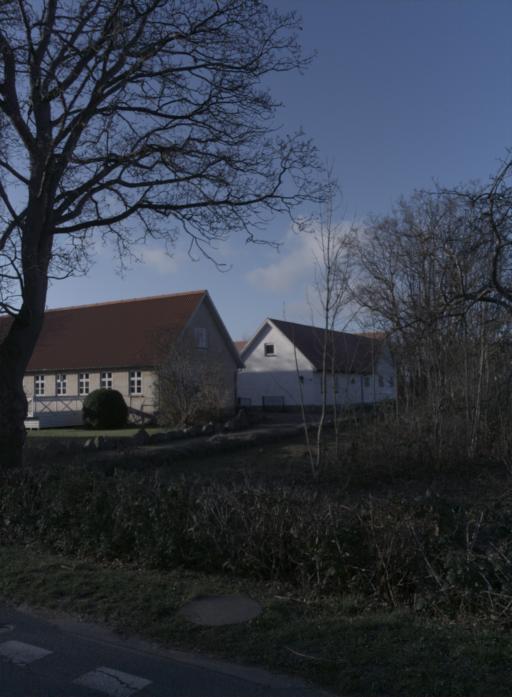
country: DK
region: Zealand
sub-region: Kalundborg Kommune
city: Kalundborg
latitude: 55.6910
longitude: 11.1433
